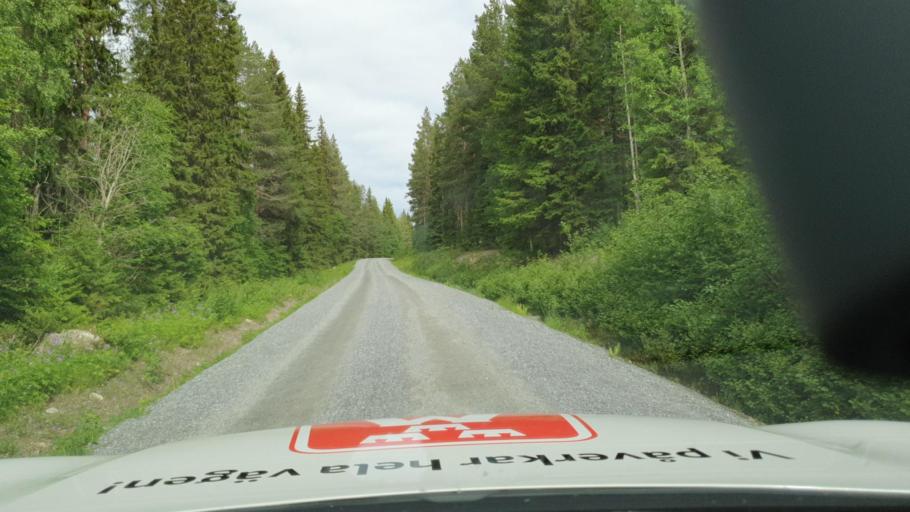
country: SE
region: Vaesterbotten
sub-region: Skelleftea Kommun
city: Langsele
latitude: 64.5885
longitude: 20.2975
